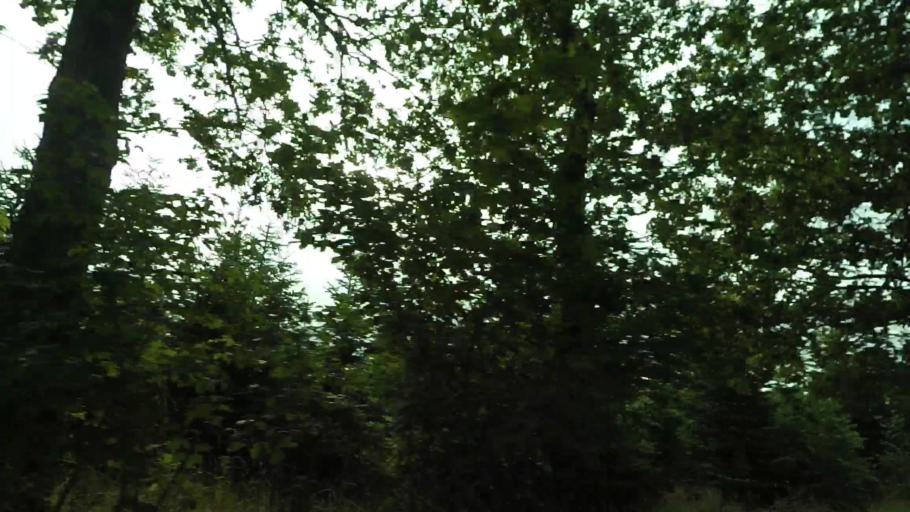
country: DK
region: Central Jutland
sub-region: Syddjurs Kommune
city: Ronde
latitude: 56.3408
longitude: 10.4857
